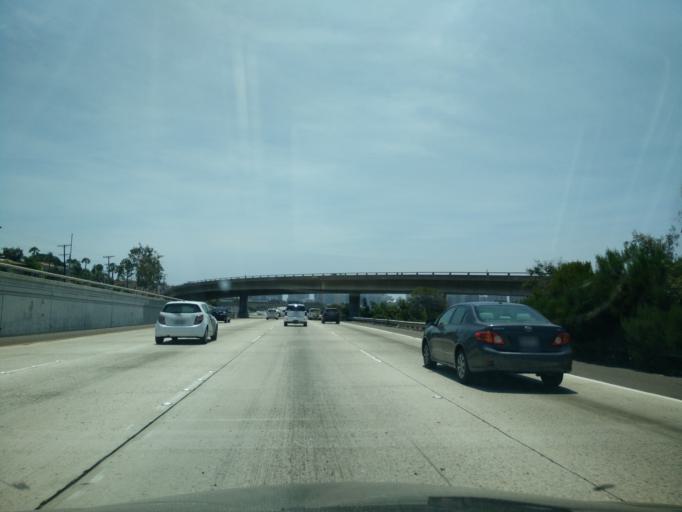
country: US
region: California
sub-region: San Diego County
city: San Diego
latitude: 32.7362
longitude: -117.1758
